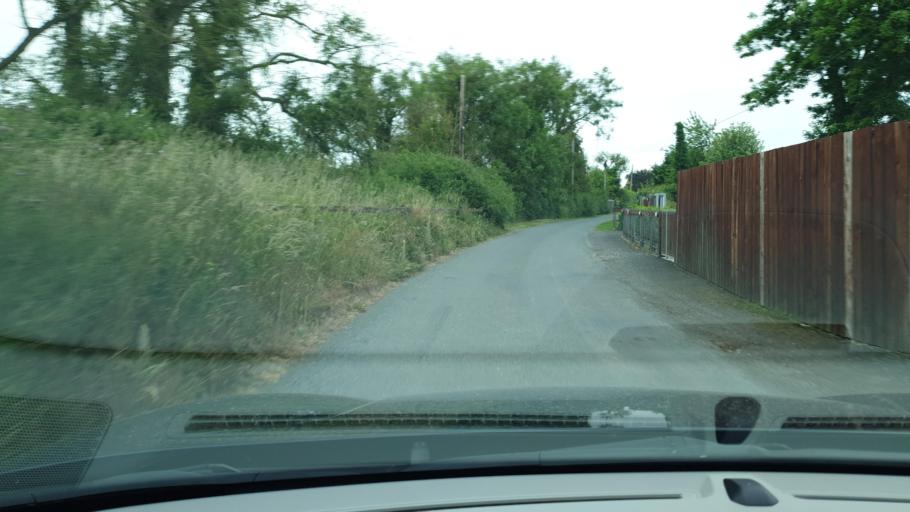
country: IE
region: Leinster
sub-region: An Mhi
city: Ashbourne
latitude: 53.4801
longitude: -6.4014
